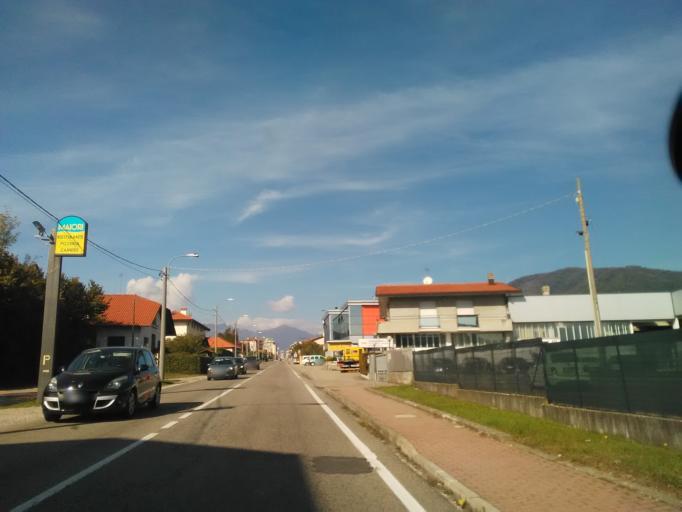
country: IT
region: Piedmont
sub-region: Provincia di Vercelli
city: Serravalle Sesia
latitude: 45.6781
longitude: 8.3189
